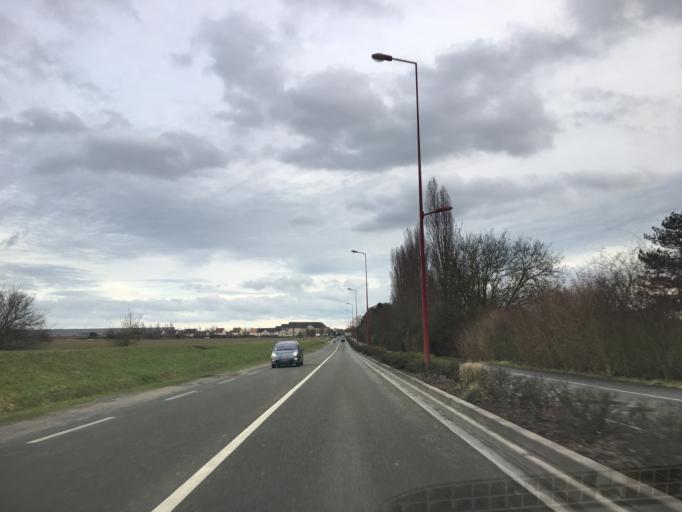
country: FR
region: Ile-de-France
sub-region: Departement du Val-d'Oise
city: Gonesse
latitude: 48.9964
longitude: 2.4377
